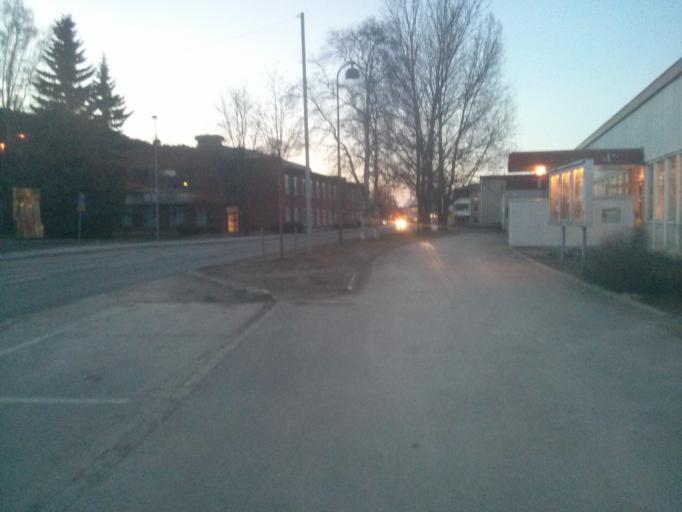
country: SE
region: Vaesternorrland
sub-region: Sundsvalls Kommun
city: Kvissleby
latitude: 62.2960
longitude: 17.3792
